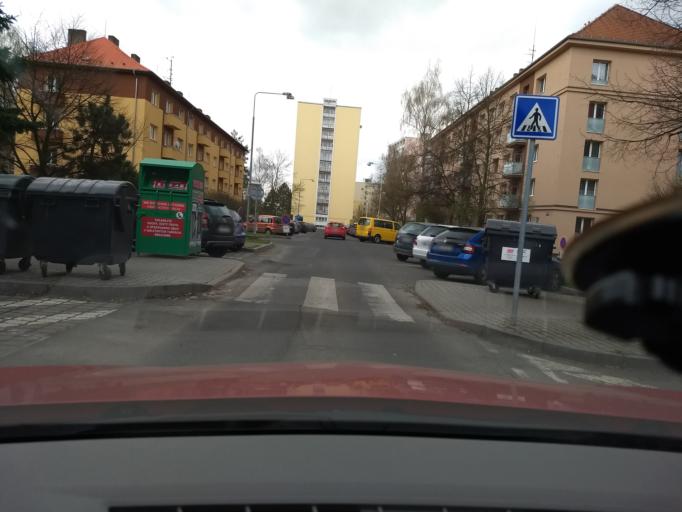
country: CZ
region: Central Bohemia
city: Kladno
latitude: 50.1324
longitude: 14.1220
